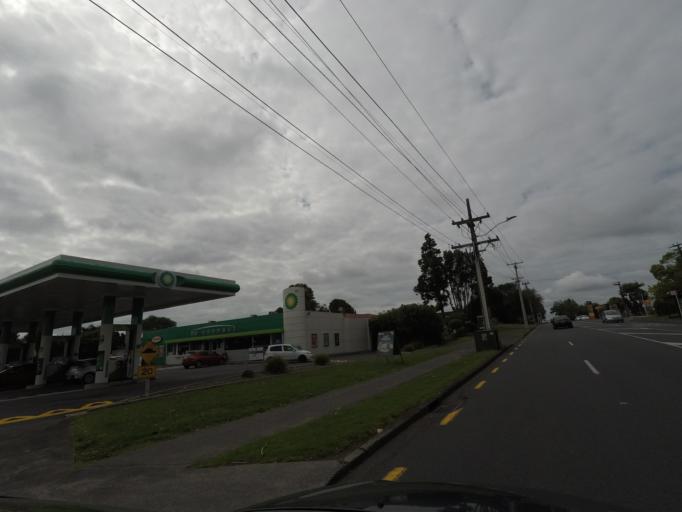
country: NZ
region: Auckland
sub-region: Auckland
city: Rosebank
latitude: -36.8637
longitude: 174.6147
